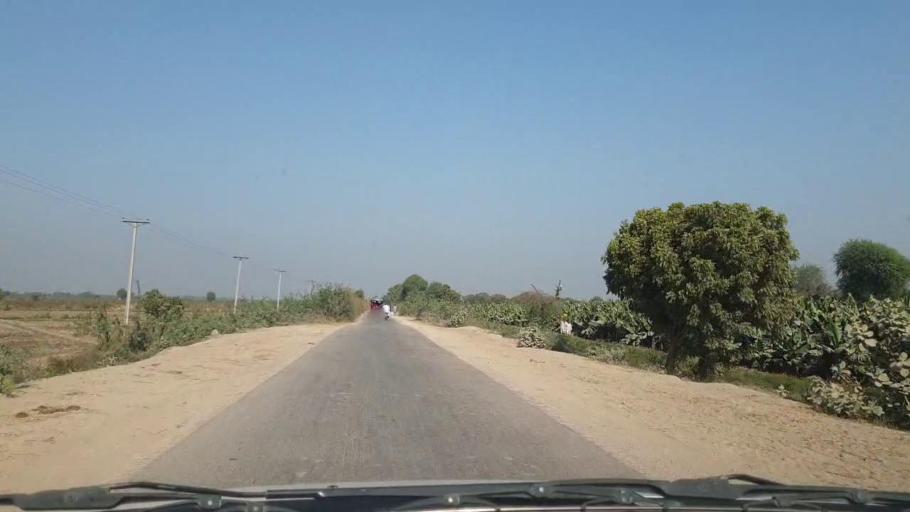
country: PK
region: Sindh
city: Tando Muhammad Khan
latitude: 25.1704
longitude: 68.5899
